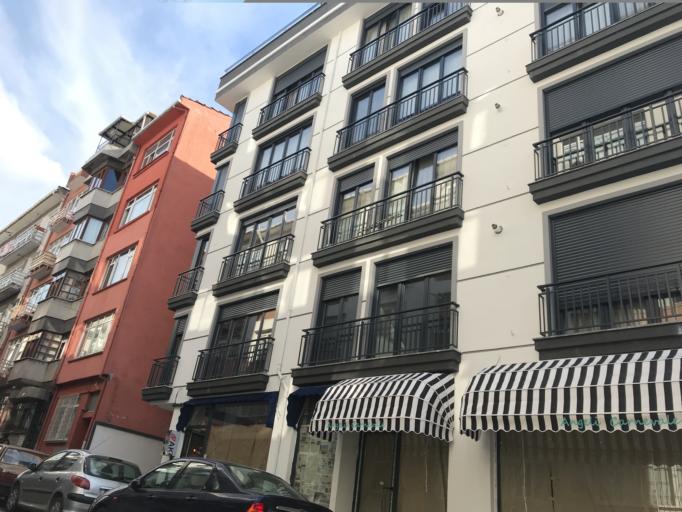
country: TR
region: Istanbul
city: UEskuedar
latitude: 40.9860
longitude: 29.0229
